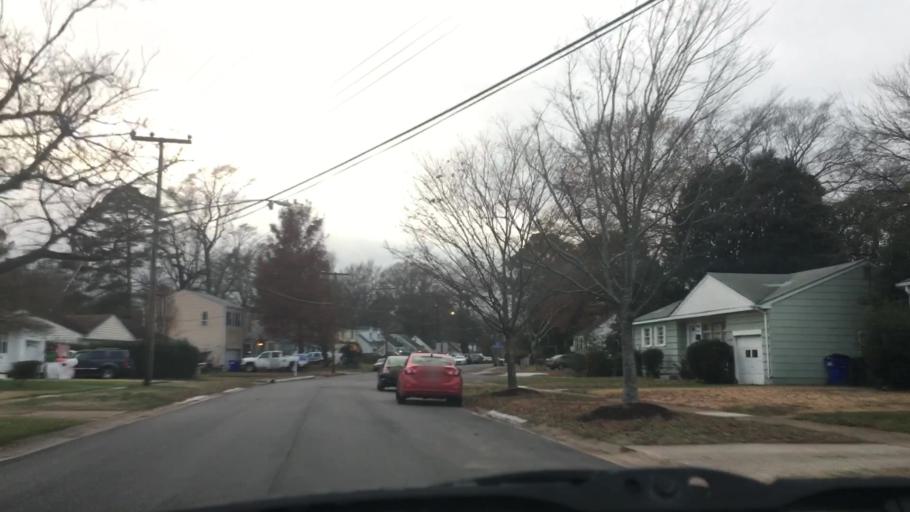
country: US
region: Virginia
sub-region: City of Norfolk
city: Norfolk
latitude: 36.9288
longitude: -76.2344
